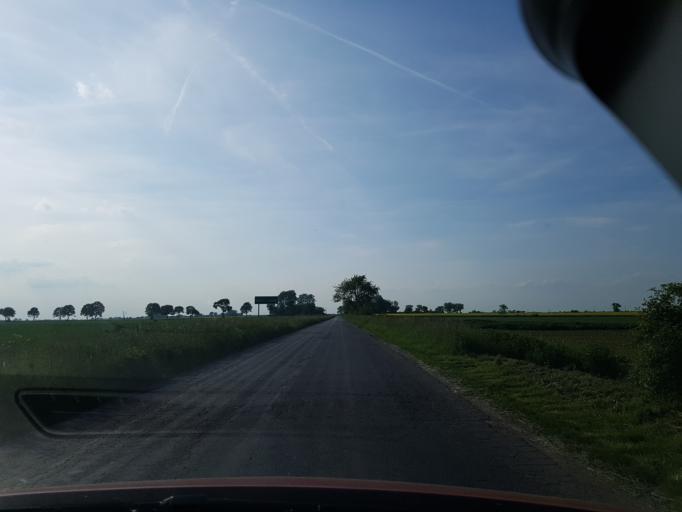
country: PL
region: Lower Silesian Voivodeship
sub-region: Powiat strzelinski
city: Wiazow
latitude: 50.8564
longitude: 17.1825
